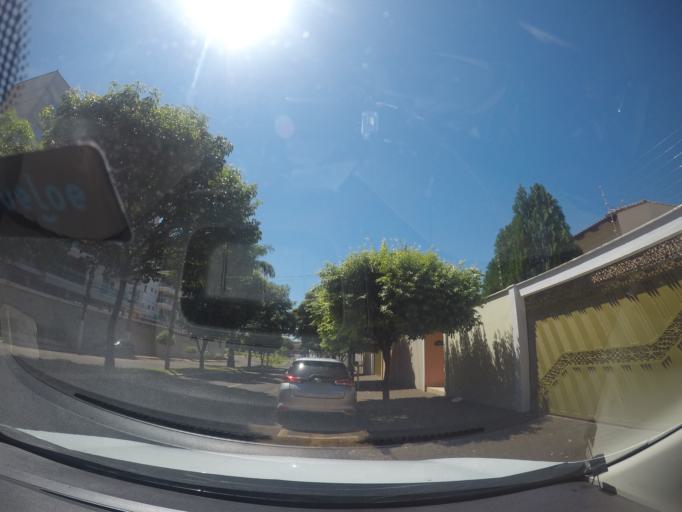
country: BR
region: Goias
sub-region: Itumbiara
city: Itumbiara
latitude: -18.4103
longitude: -49.2034
